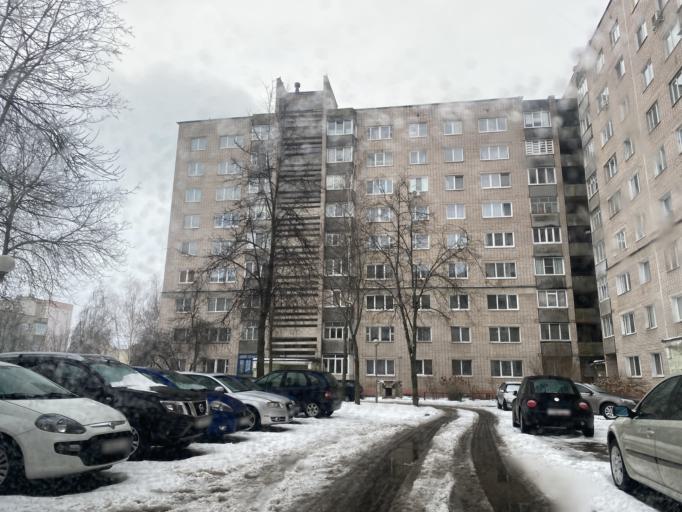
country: BY
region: Minsk
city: Horad Zhodzina
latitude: 54.0941
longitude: 28.3049
